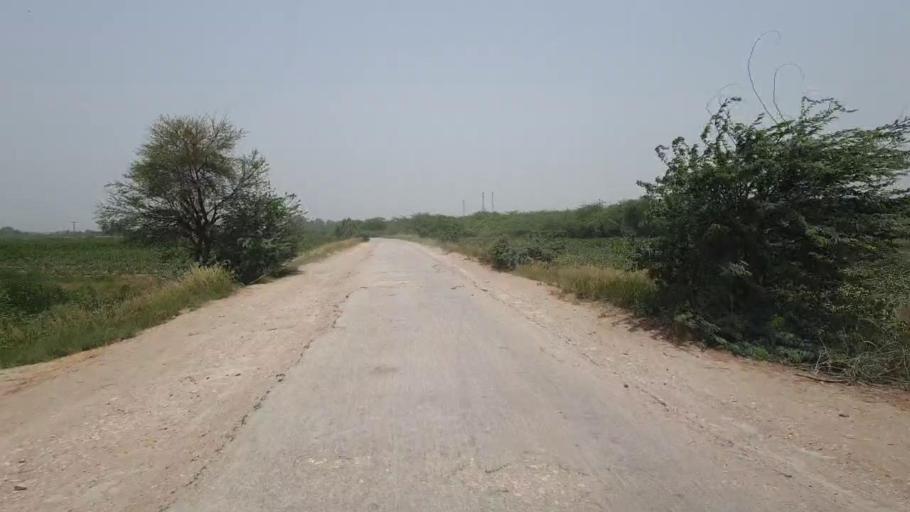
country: PK
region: Sindh
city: Tando Mittha Khan
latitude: 26.0665
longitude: 69.1995
